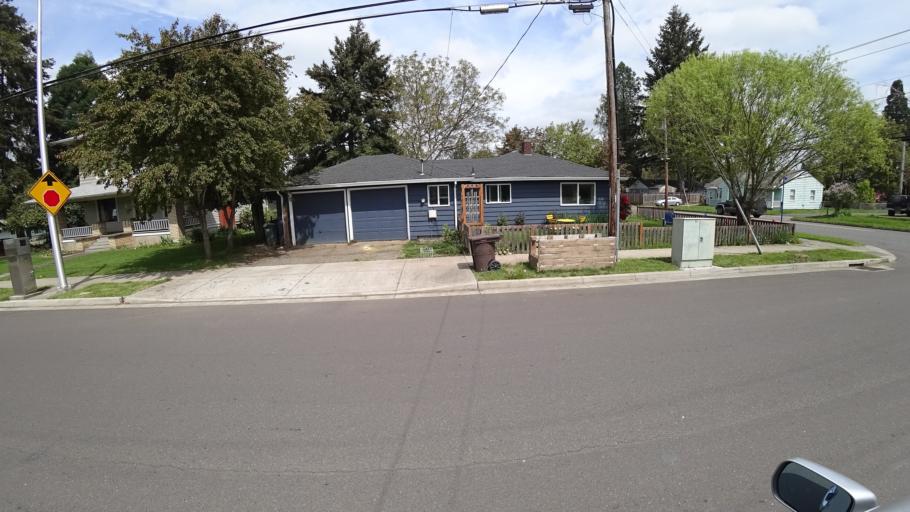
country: US
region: Oregon
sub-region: Washington County
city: Hillsboro
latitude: 45.5277
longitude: -122.9900
